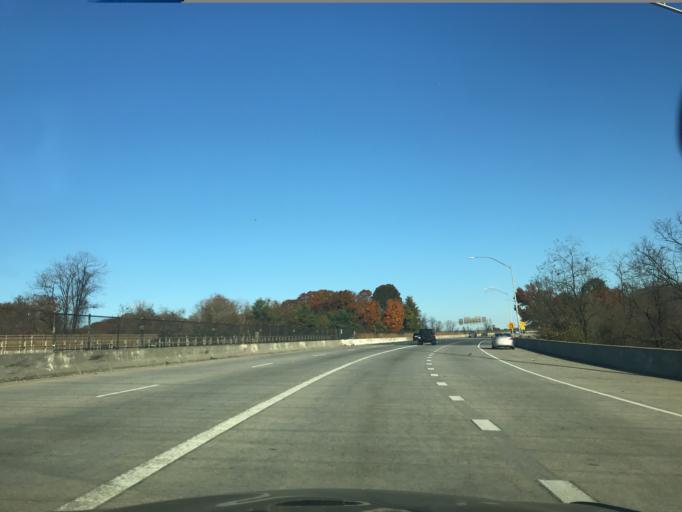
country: US
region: Maryland
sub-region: Baltimore County
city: Pikesville
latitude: 39.3760
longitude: -76.7514
